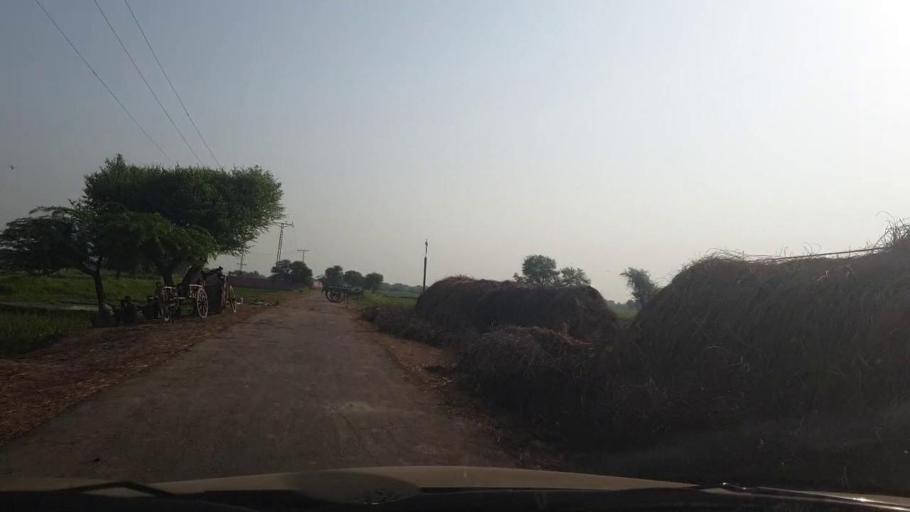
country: PK
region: Sindh
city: Larkana
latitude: 27.5770
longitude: 68.1528
